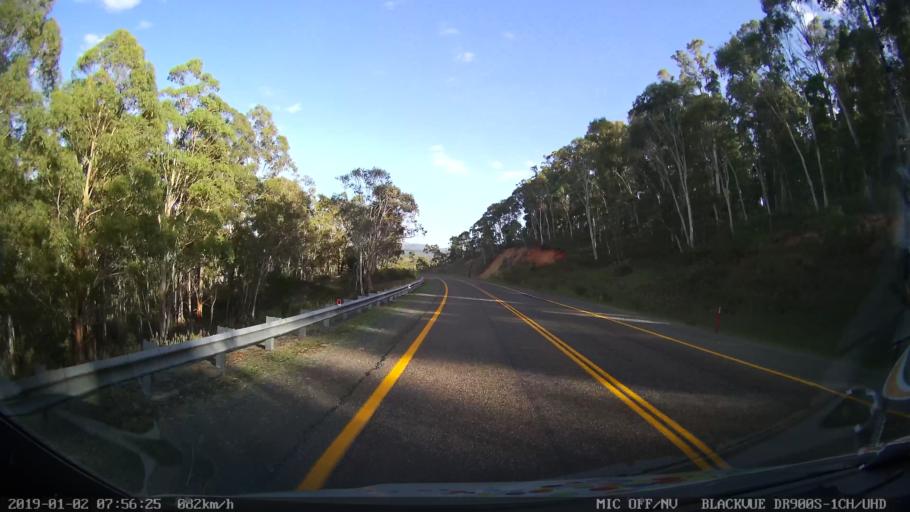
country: AU
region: New South Wales
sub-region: Tumut Shire
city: Tumut
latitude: -35.6709
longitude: 148.4853
